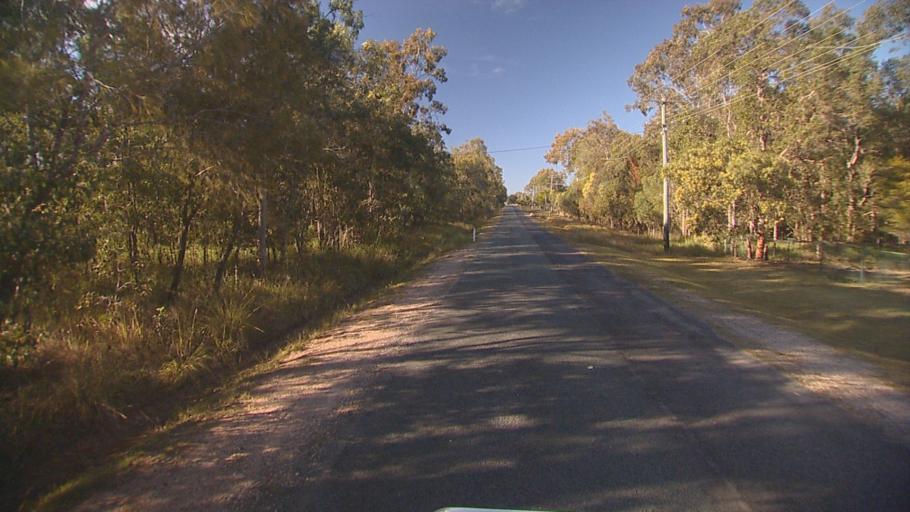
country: AU
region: Queensland
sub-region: Logan
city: Park Ridge South
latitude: -27.7200
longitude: 152.9820
